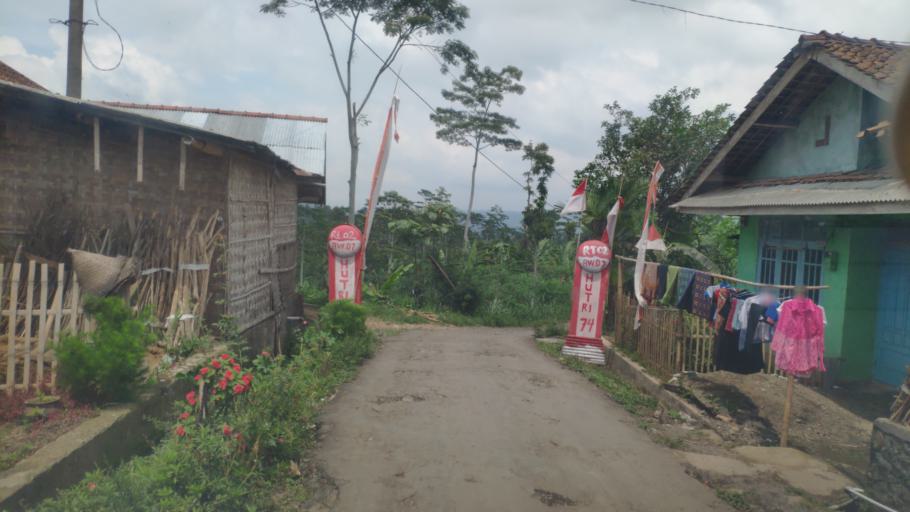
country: ID
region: Central Java
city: Wonosobo
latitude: -7.2705
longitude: 109.8054
